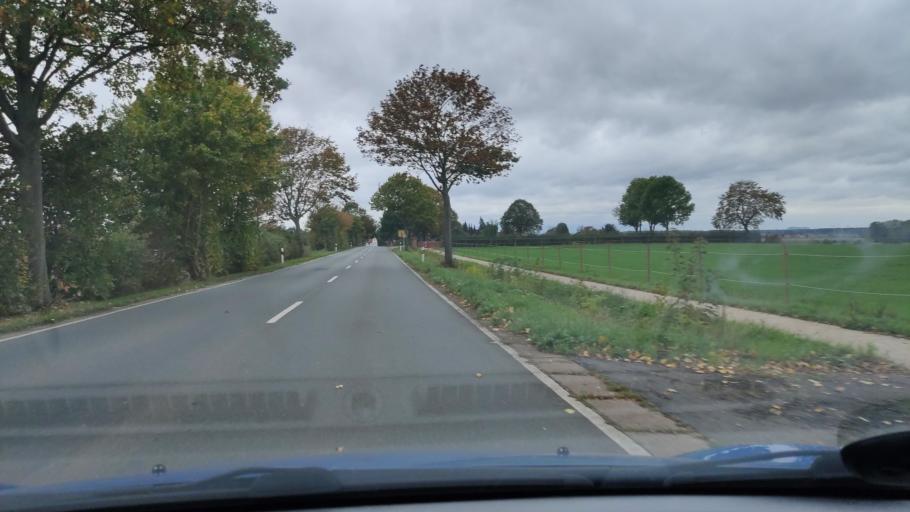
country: DE
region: Lower Saxony
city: Seelze
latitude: 52.3748
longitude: 9.5983
